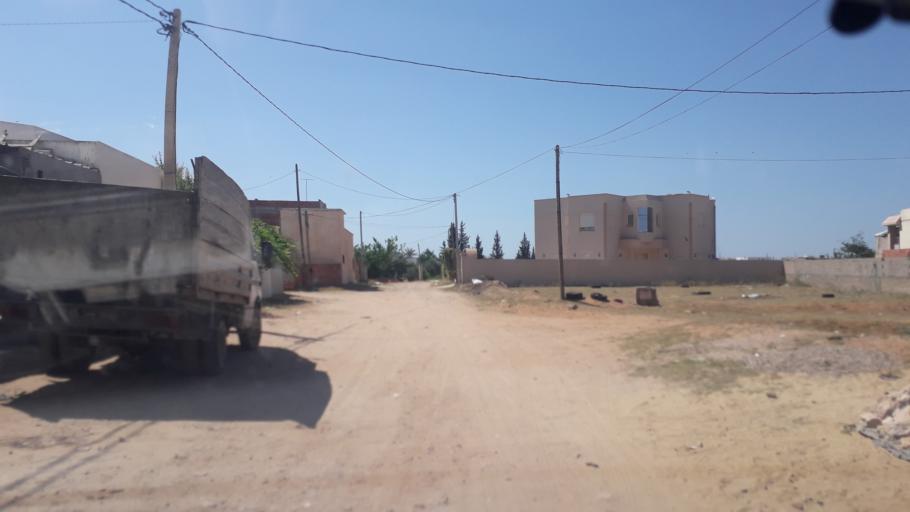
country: TN
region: Safaqis
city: Al Qarmadah
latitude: 34.8274
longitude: 10.7670
